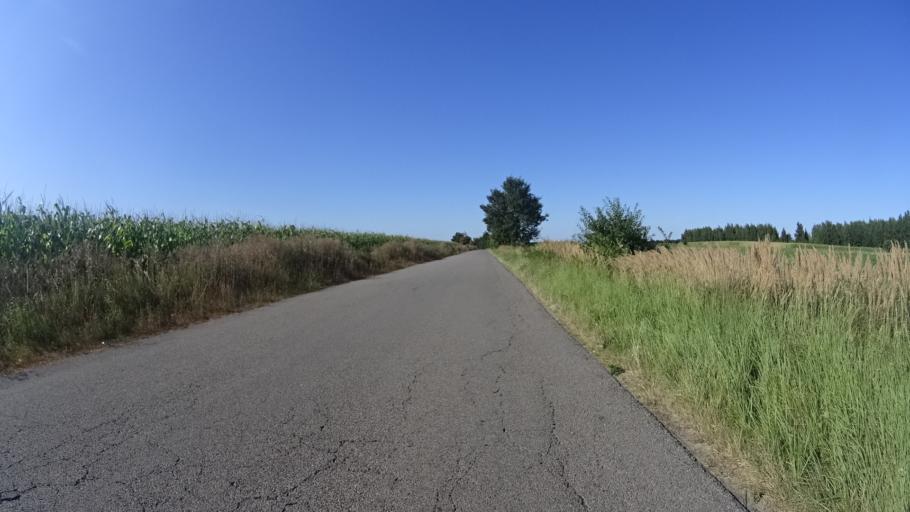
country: PL
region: Masovian Voivodeship
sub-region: Powiat bialobrzeski
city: Wysmierzyce
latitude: 51.6670
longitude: 20.8313
